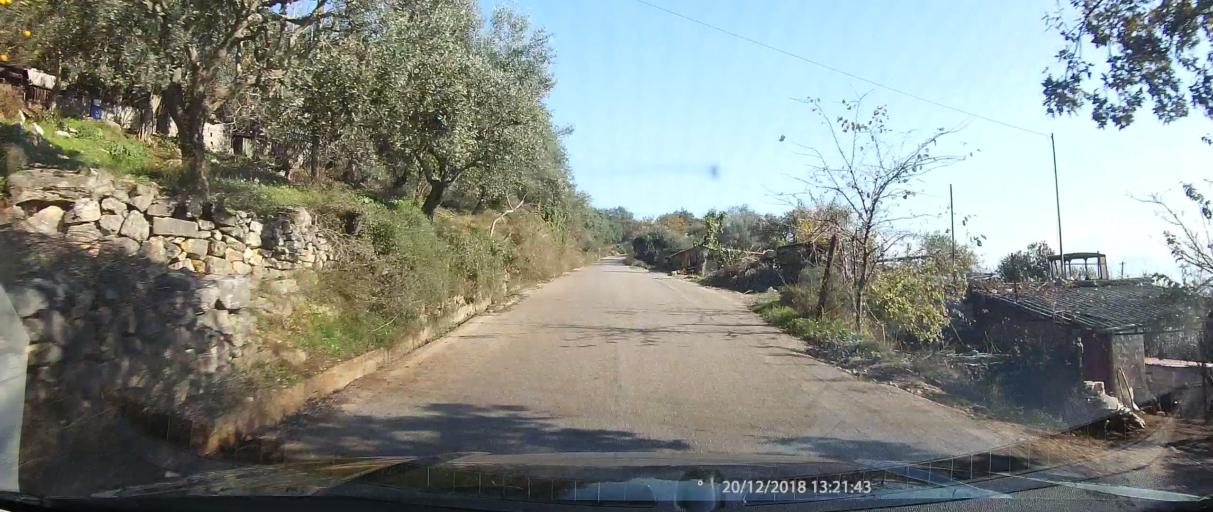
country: GR
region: West Greece
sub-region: Nomos Aitolias kai Akarnanias
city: Paravola
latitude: 38.6166
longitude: 21.5588
